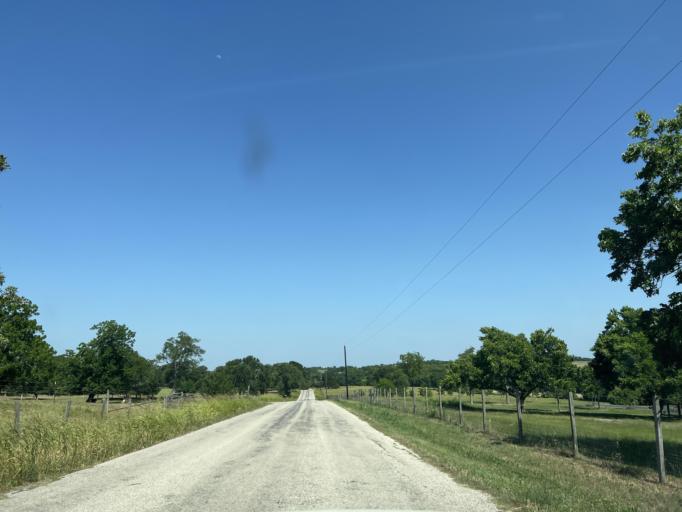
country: US
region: Texas
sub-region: Washington County
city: Brenham
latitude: 30.1751
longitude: -96.3477
